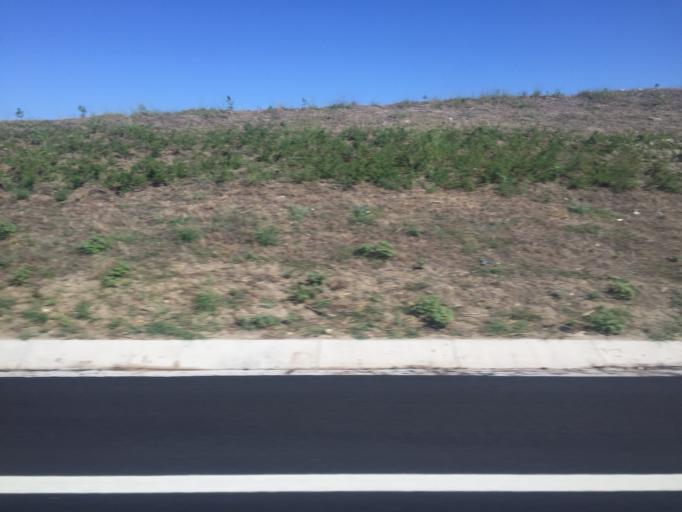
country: TR
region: Bursa
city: Gorukle
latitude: 40.2435
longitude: 28.7777
